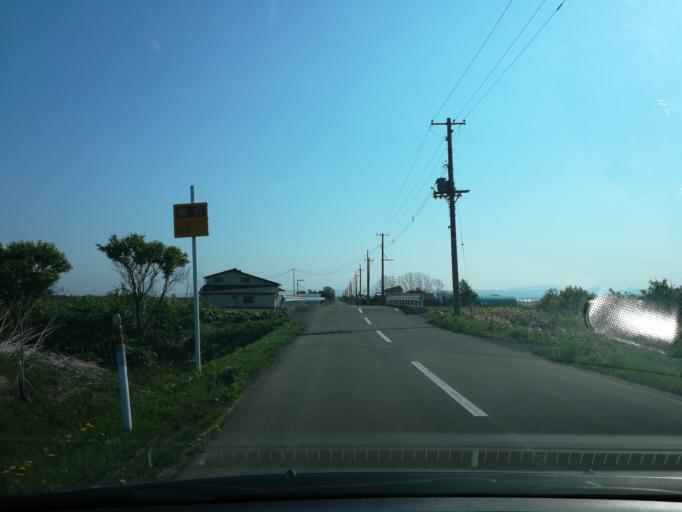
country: JP
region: Hokkaido
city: Ebetsu
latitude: 43.1259
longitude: 141.6663
